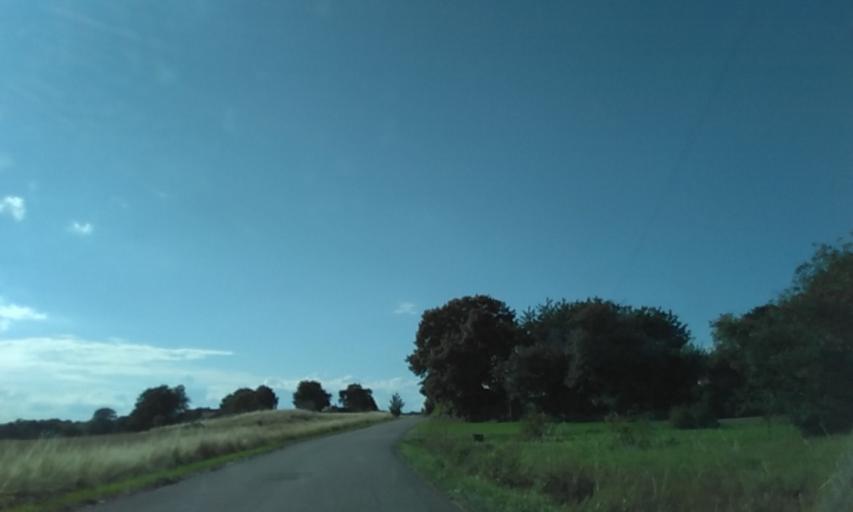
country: SE
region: Vaestra Goetaland
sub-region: Lidkopings Kommun
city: Lidkoping
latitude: 58.5728
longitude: 13.0313
